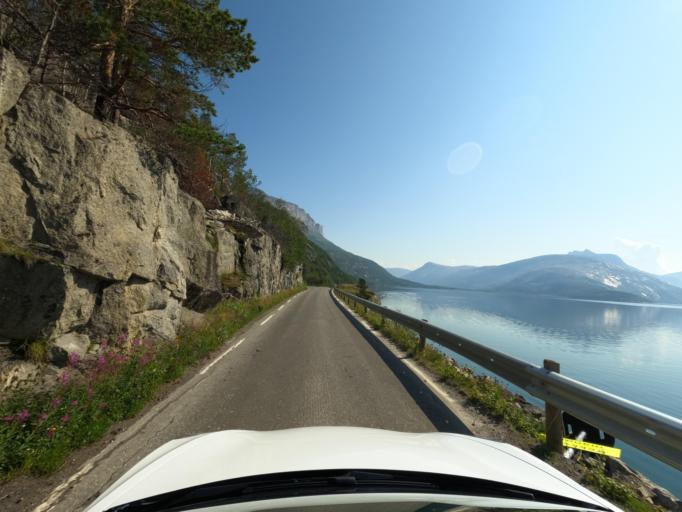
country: NO
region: Nordland
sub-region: Narvik
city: Narvik
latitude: 68.2913
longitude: 17.3585
